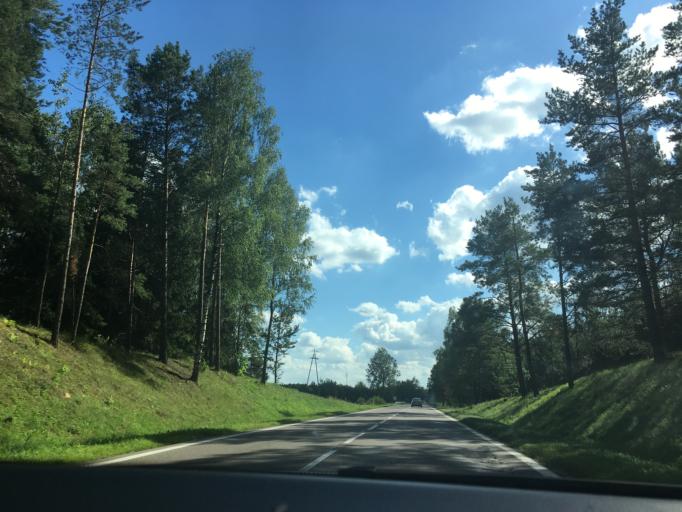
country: PL
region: Podlasie
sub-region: Powiat sokolski
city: Janow
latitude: 53.3531
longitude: 23.1000
